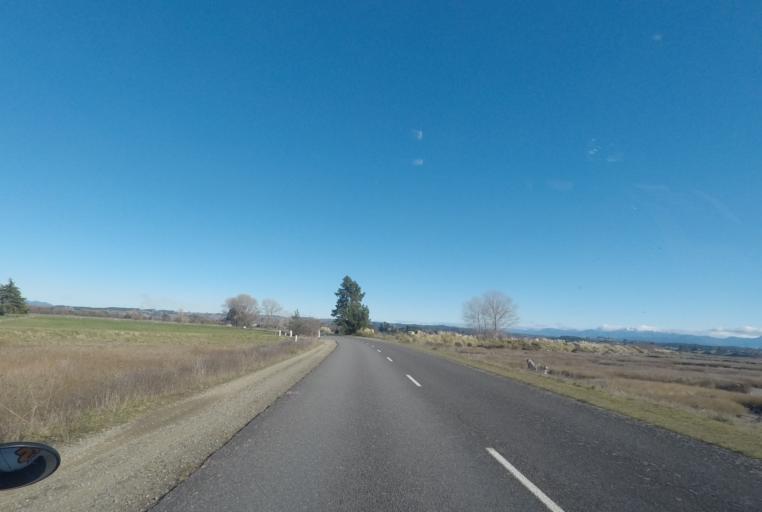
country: NZ
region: Tasman
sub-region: Tasman District
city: Mapua
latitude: -41.2870
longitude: 173.1271
